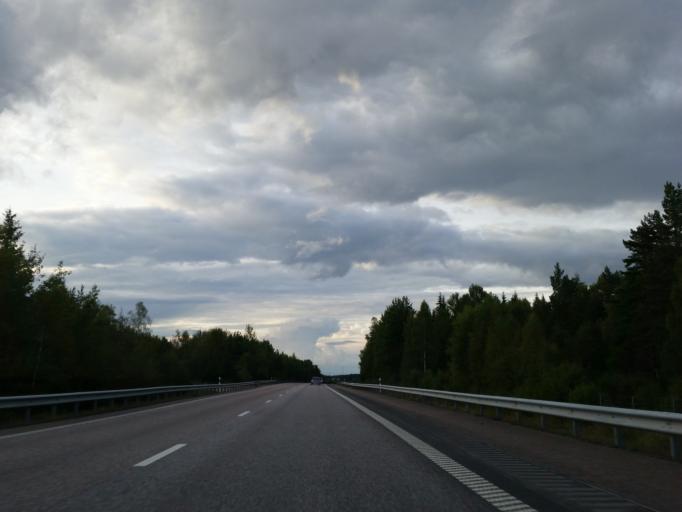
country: SE
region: Stockholm
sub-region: Sigtuna Kommun
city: Marsta
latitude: 59.6680
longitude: 17.8772
